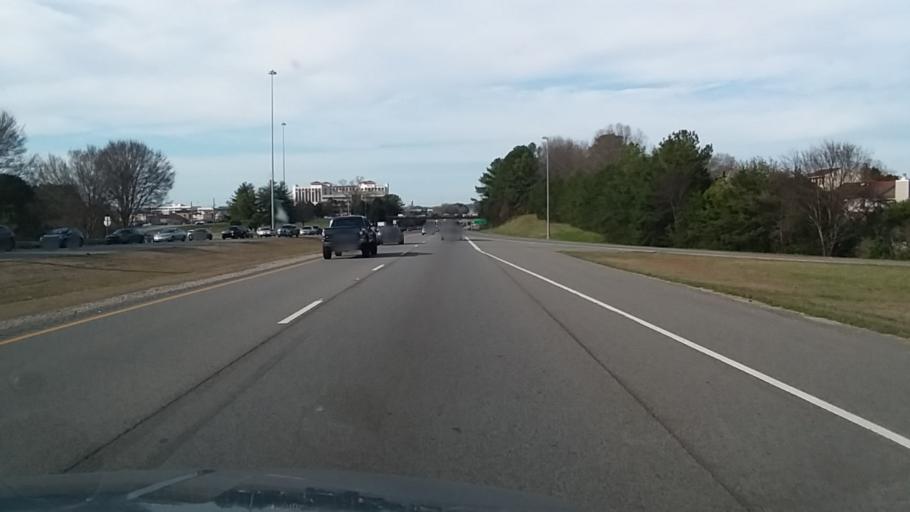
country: US
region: Alabama
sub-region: Madison County
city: Redstone Arsenal
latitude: 34.7095
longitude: -86.6710
